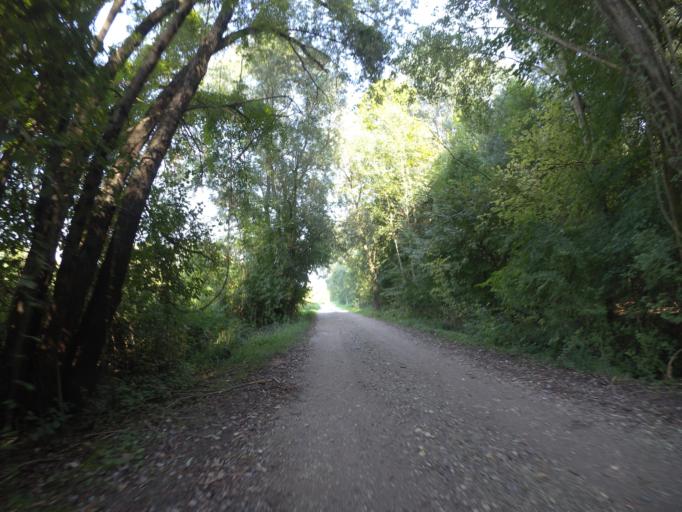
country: IT
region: Friuli Venezia Giulia
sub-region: Provincia di Udine
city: Varmo
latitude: 45.8829
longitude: 12.9764
